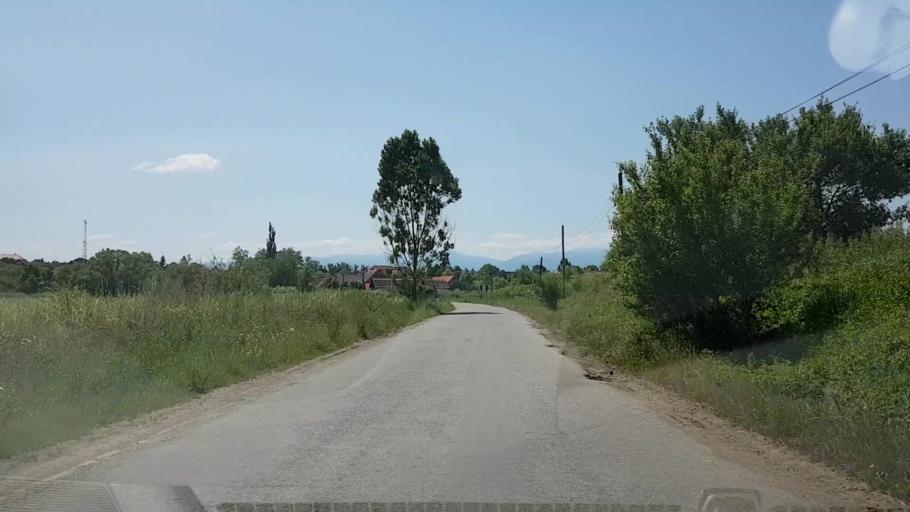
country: RO
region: Brasov
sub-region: Comuna Cincu
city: Cincu
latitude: 45.9216
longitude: 24.7983
